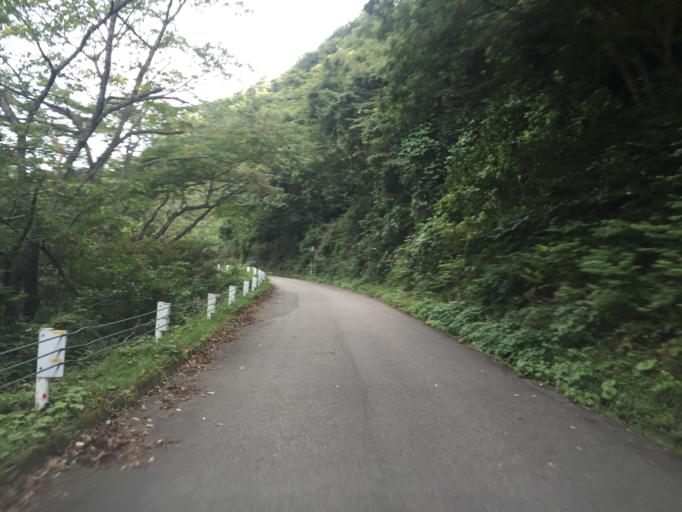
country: JP
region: Fukushima
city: Inawashiro
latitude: 37.4822
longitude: 139.9780
